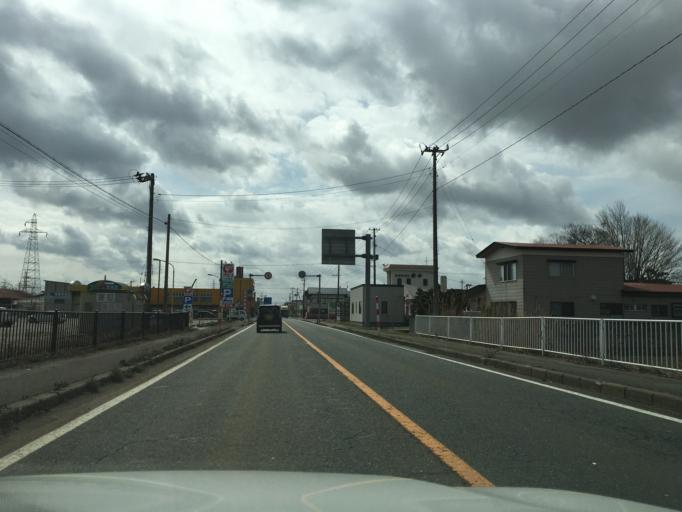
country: JP
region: Akita
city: Tenno
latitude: 39.9475
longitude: 140.0835
